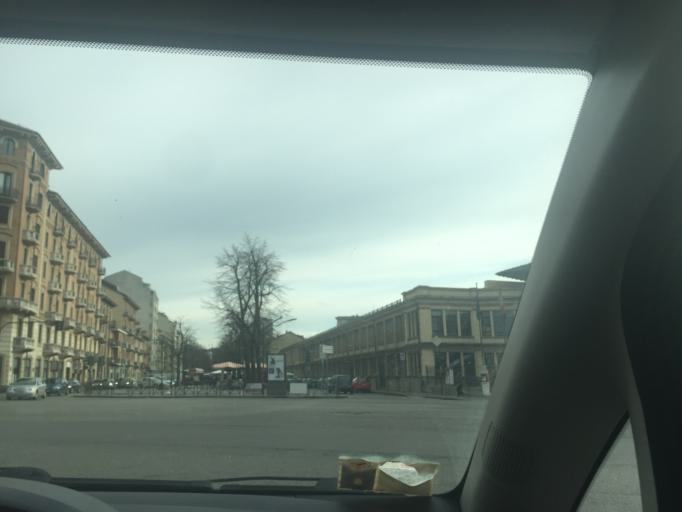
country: IT
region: Piedmont
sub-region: Provincia di Torino
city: Lesna
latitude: 45.0667
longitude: 7.6448
